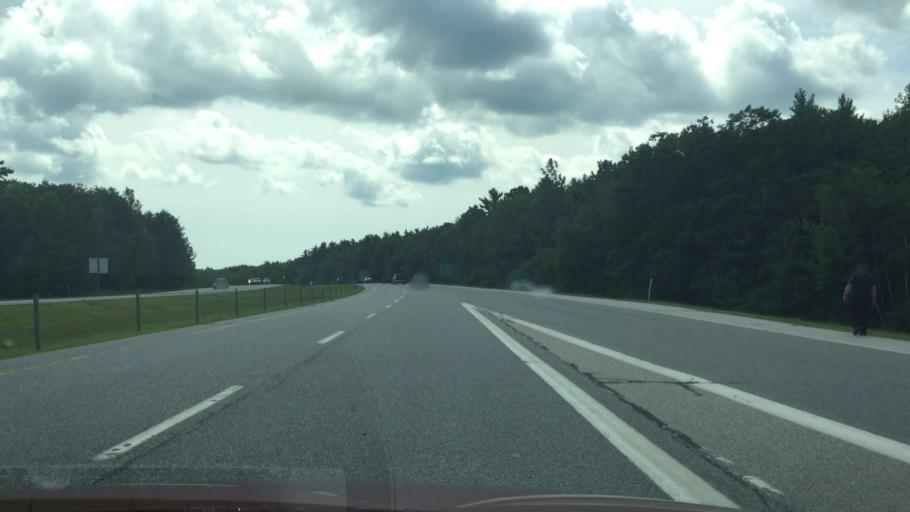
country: US
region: Maine
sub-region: York County
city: Saco
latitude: 43.5192
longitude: -70.4427
